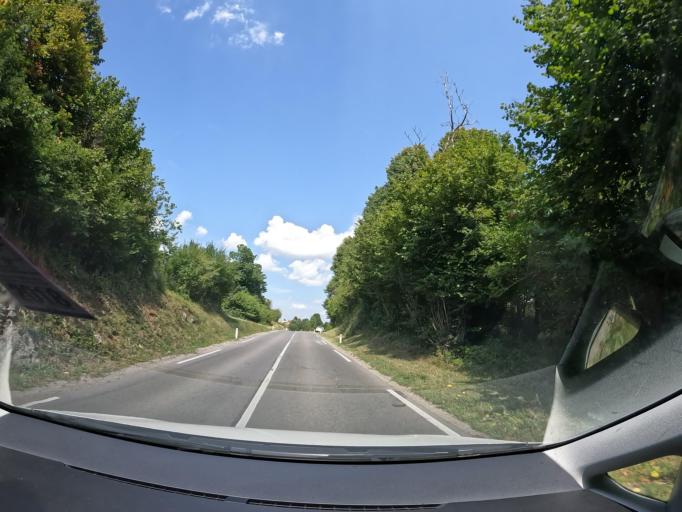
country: SI
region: Pivka
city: Pivka
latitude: 45.6507
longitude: 14.2227
